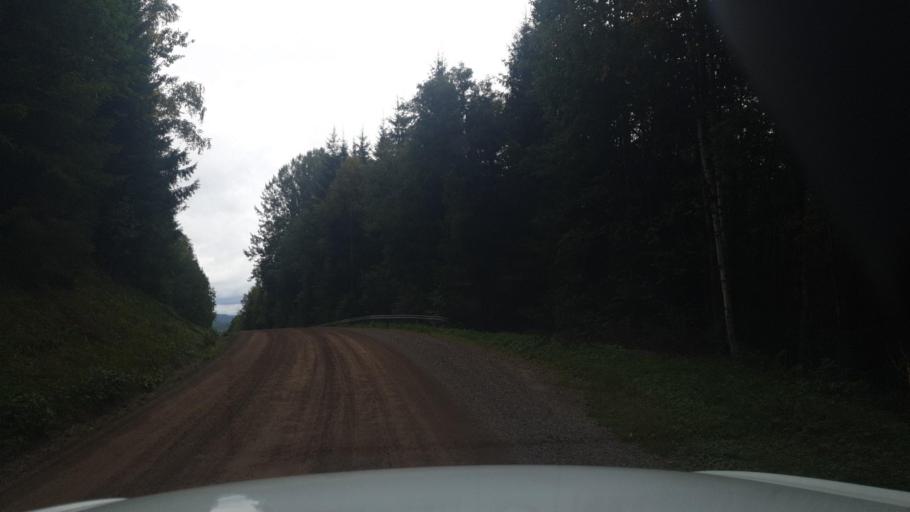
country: SE
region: Vaermland
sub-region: Arvika Kommun
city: Arvika
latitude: 60.0109
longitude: 12.6508
